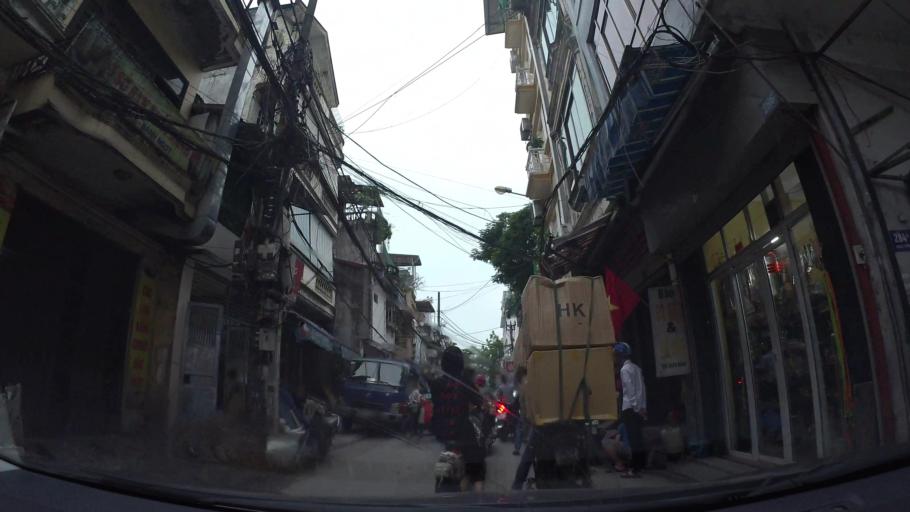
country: VN
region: Ha Noi
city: Hoan Kiem
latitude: 21.0255
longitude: 105.8618
